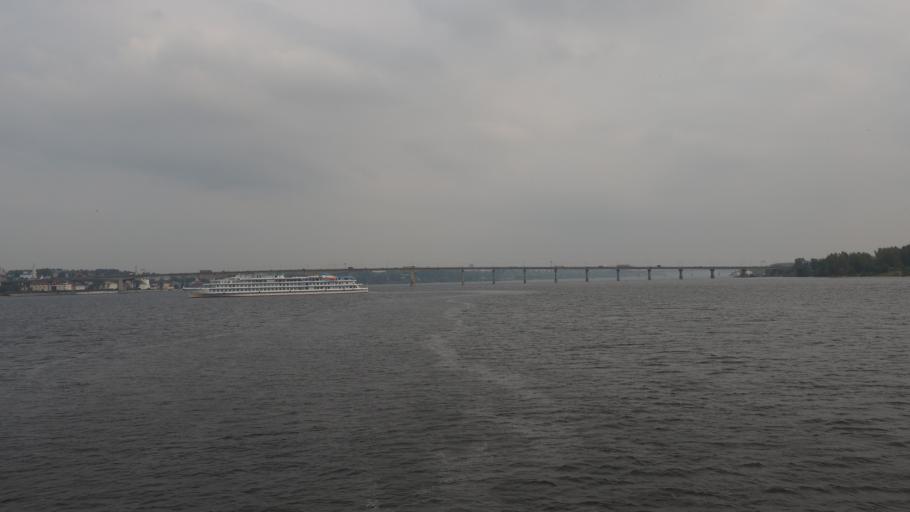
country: RU
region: Kostroma
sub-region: Kostromskoy Rayon
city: Kostroma
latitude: 57.7583
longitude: 40.9206
